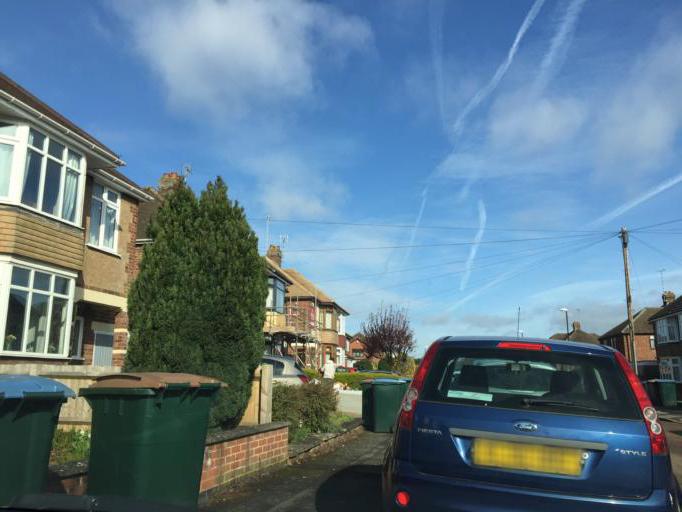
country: GB
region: England
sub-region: Coventry
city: Coventry
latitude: 52.3809
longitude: -1.5079
